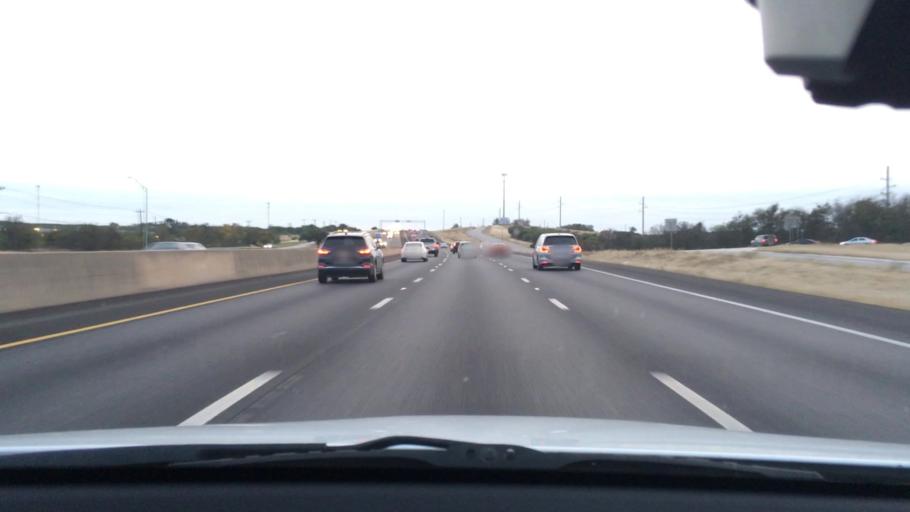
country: US
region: Texas
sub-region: Hays County
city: Kyle
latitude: 29.9828
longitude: -97.8732
